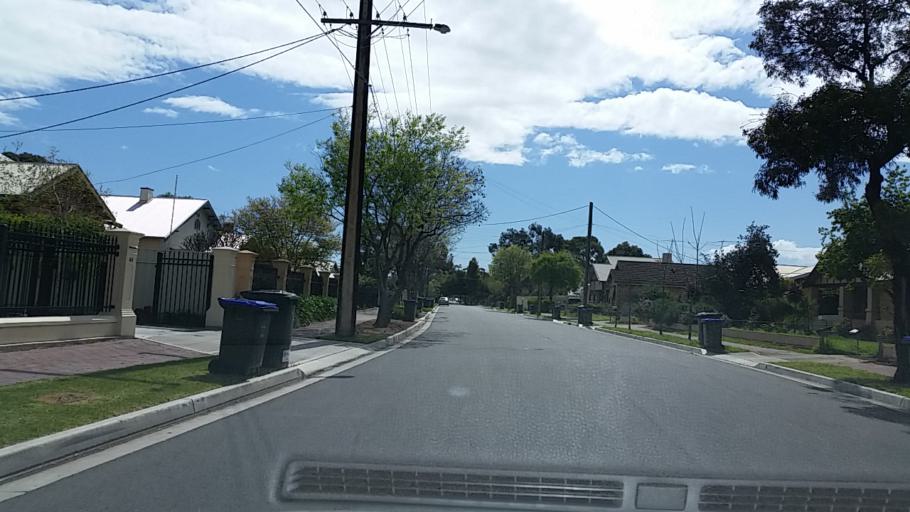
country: AU
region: South Australia
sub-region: Charles Sturt
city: Woodville
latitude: -34.8808
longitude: 138.5453
